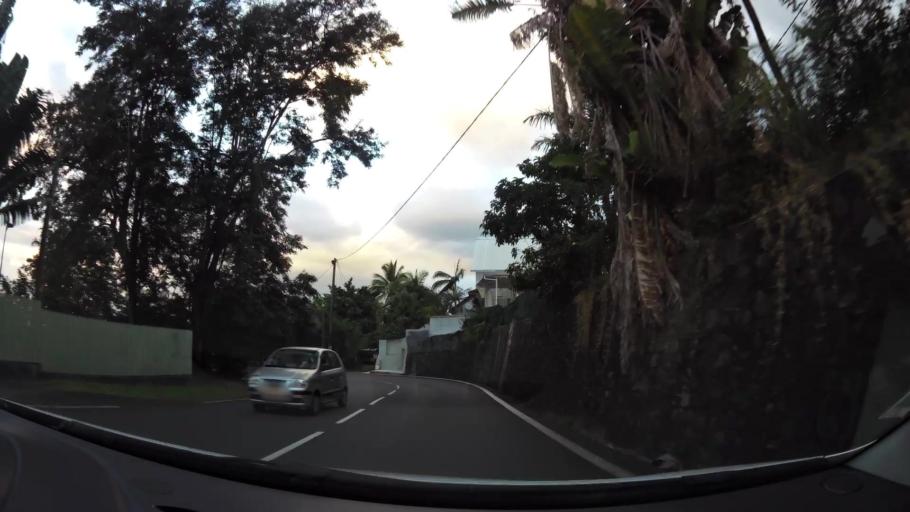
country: RE
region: Reunion
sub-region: Reunion
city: Saint-Denis
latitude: -20.9034
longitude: 55.4632
